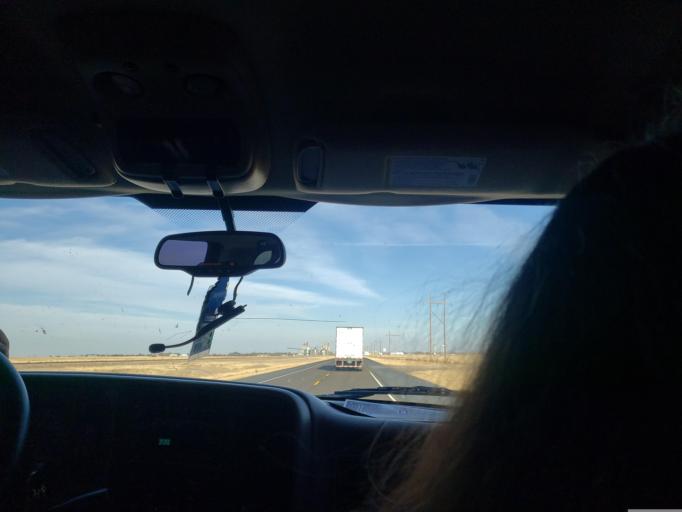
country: US
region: Oklahoma
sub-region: Texas County
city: Goodwell
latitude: 36.4874
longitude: -101.8087
